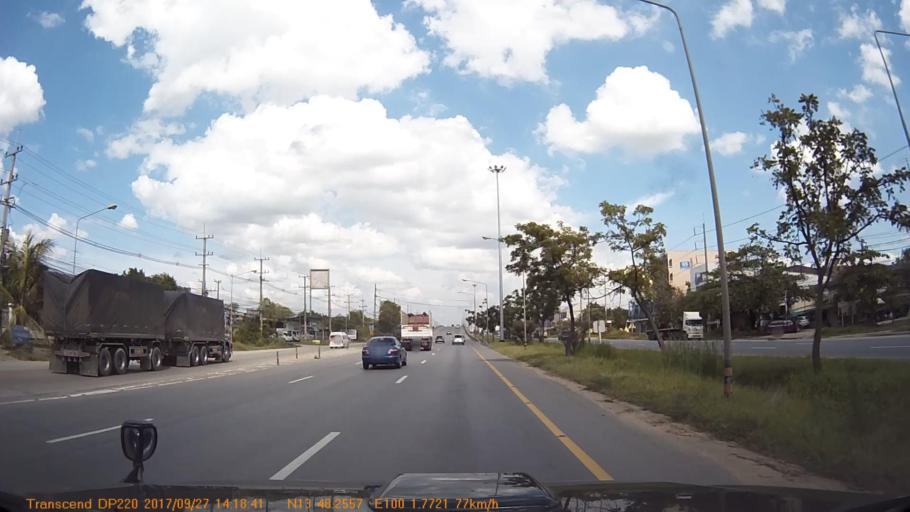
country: TH
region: Nakhon Pathom
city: Nakhon Pathom
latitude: 13.8043
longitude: 100.0296
